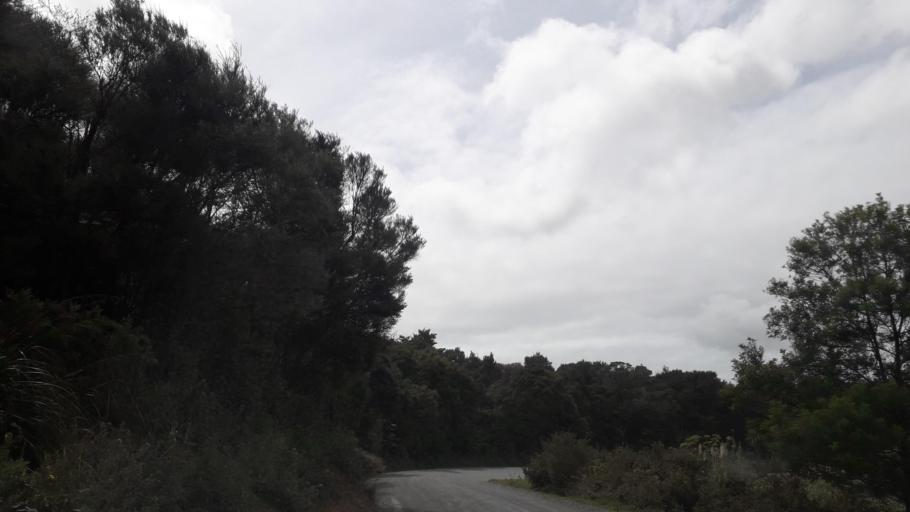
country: NZ
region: Northland
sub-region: Far North District
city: Taipa
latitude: -35.0367
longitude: 173.5647
